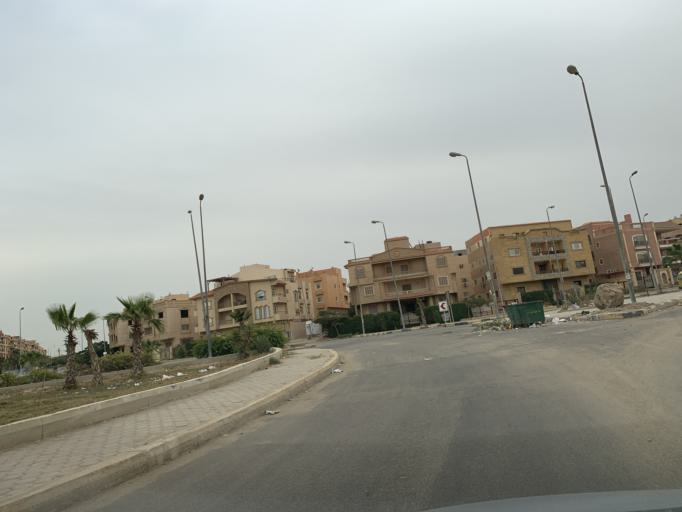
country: EG
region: Al Jizah
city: Awsim
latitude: 30.0313
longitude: 30.9797
